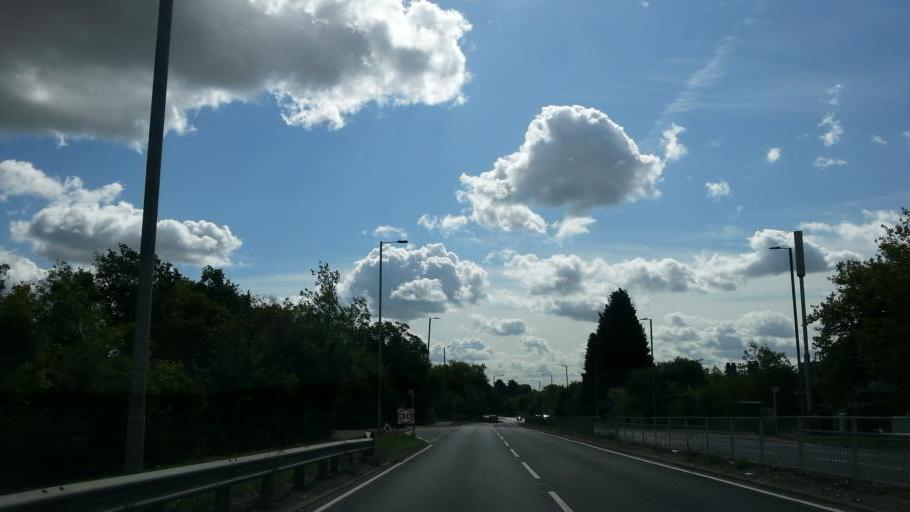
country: GB
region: England
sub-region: Essex
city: Basildon
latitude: 51.5607
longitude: 0.4536
